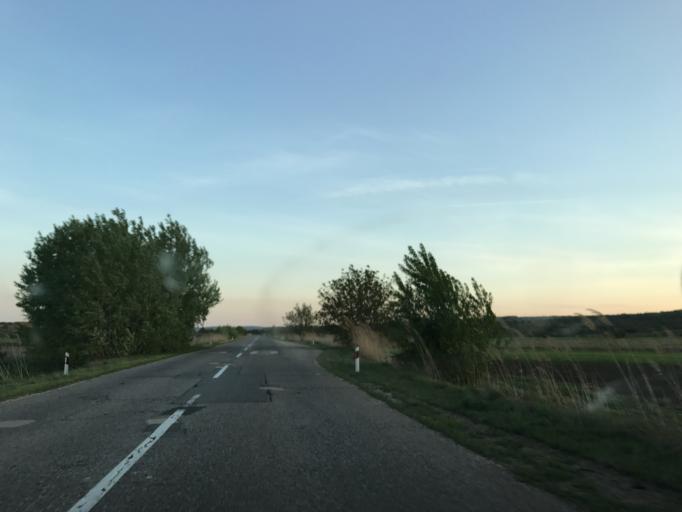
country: RS
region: Central Serbia
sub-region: Borski Okrug
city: Negotin
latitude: 44.2910
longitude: 22.5066
